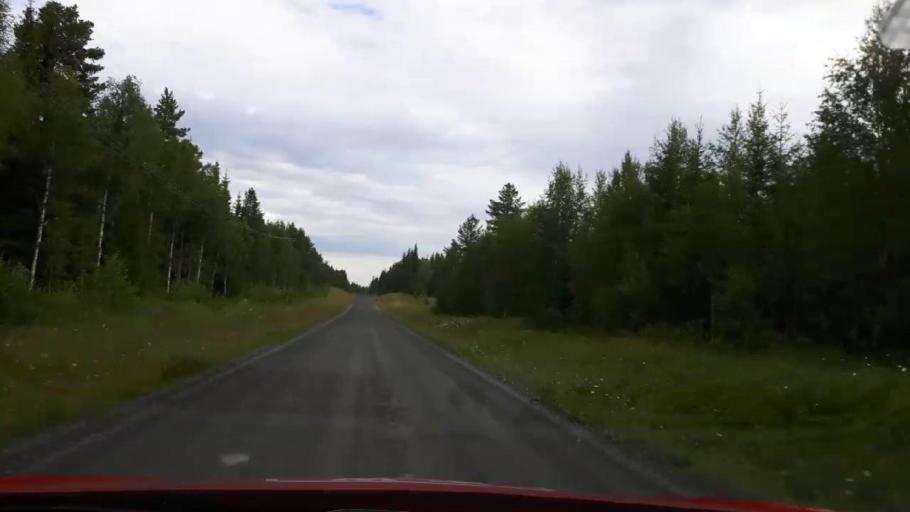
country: SE
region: Jaemtland
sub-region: Stroemsunds Kommun
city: Stroemsund
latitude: 63.5075
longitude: 15.3371
